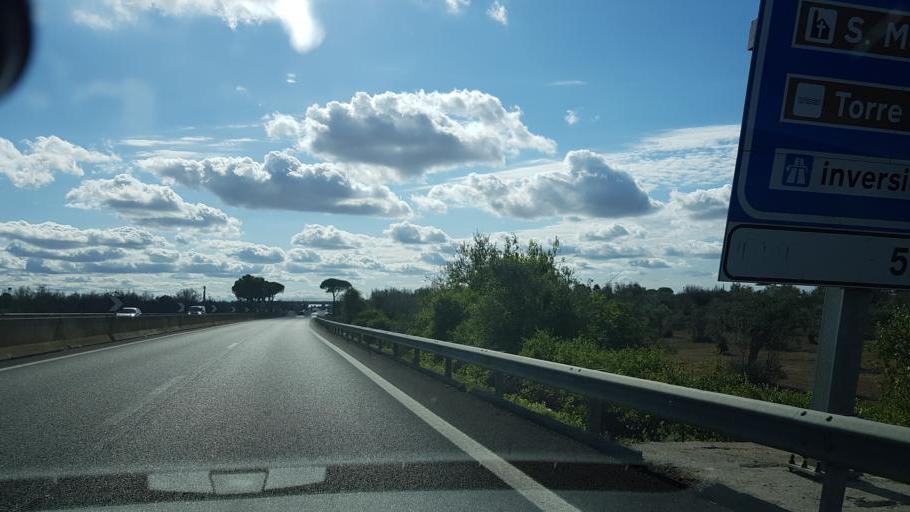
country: IT
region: Apulia
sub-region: Provincia di Lecce
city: Squinzano
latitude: 40.4449
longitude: 18.0740
